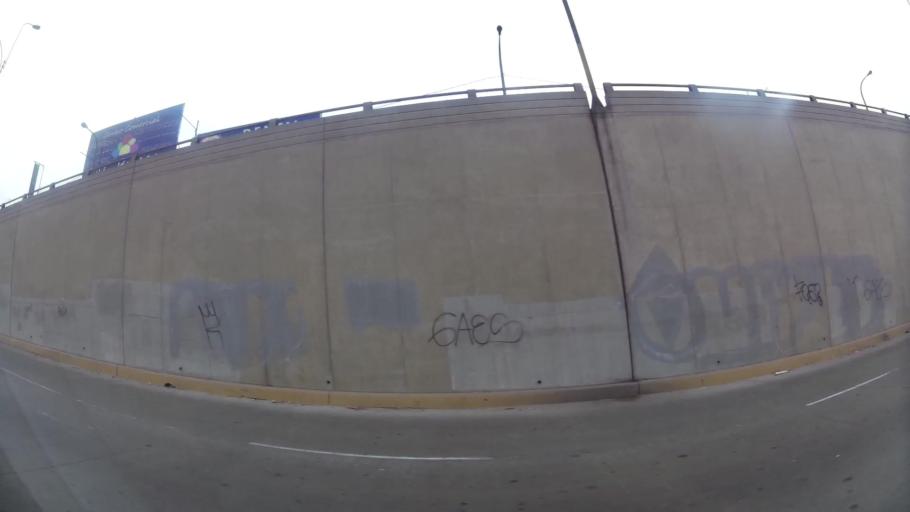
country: PE
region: Lima
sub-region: Lima
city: Vitarte
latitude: -12.0324
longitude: -76.9271
